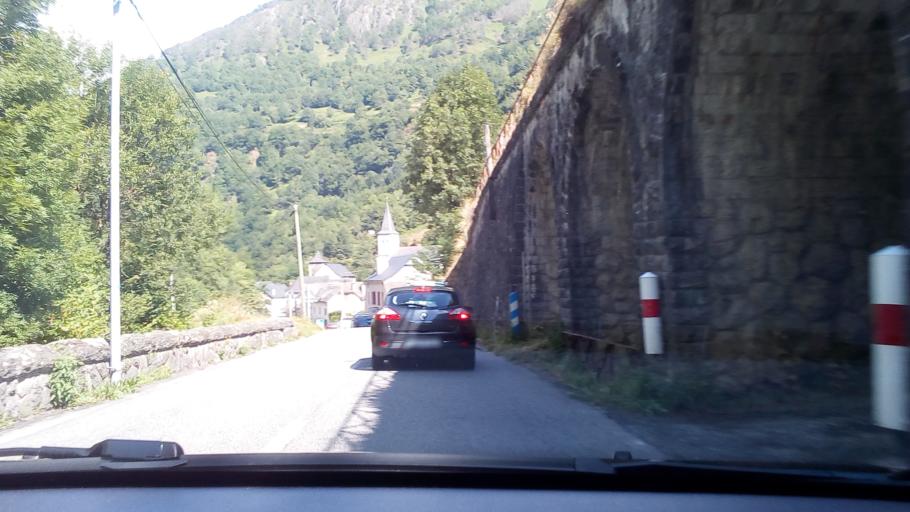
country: FR
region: Aquitaine
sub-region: Departement des Pyrenees-Atlantiques
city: Laruns
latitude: 42.9335
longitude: -0.5862
